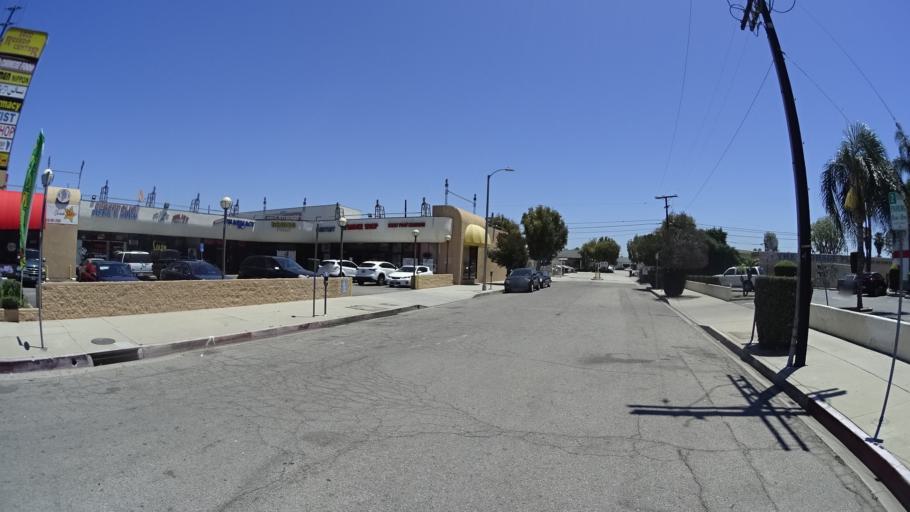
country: US
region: California
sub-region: Los Angeles County
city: Northridge
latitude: 34.1956
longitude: -118.5359
